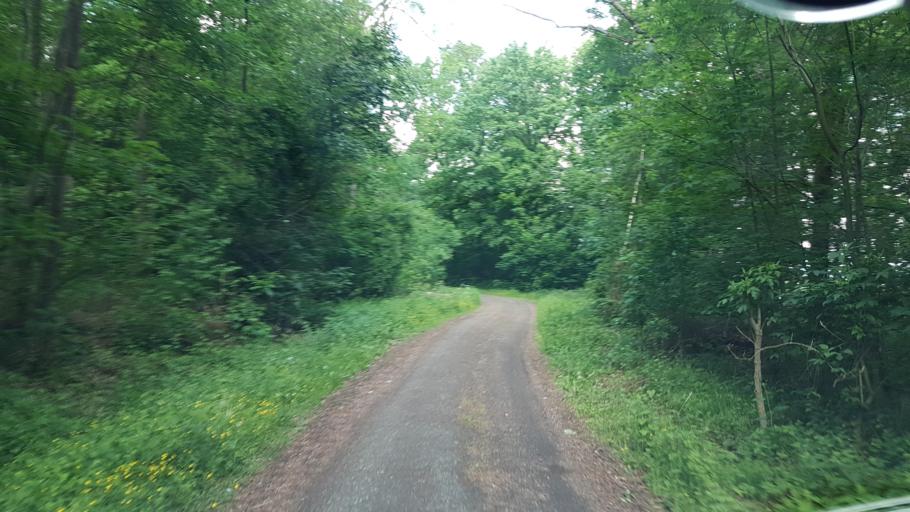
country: DE
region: Lower Saxony
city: Warberg
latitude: 52.1762
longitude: 10.9038
